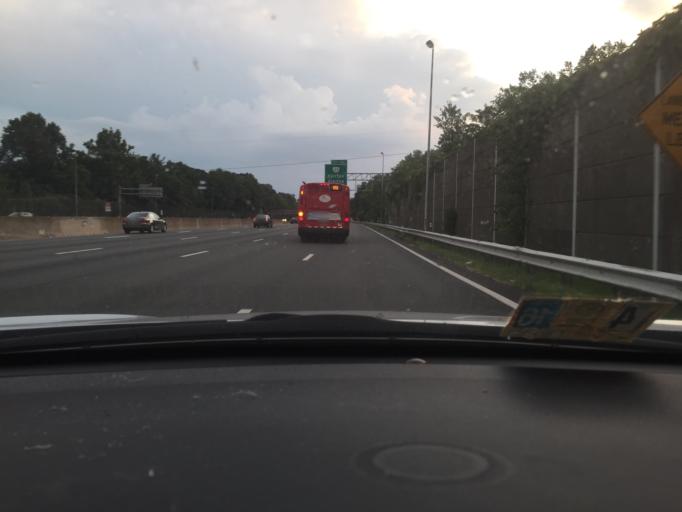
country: US
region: Virginia
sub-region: Fairfax County
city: Oakton
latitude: 38.8764
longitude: -77.2787
